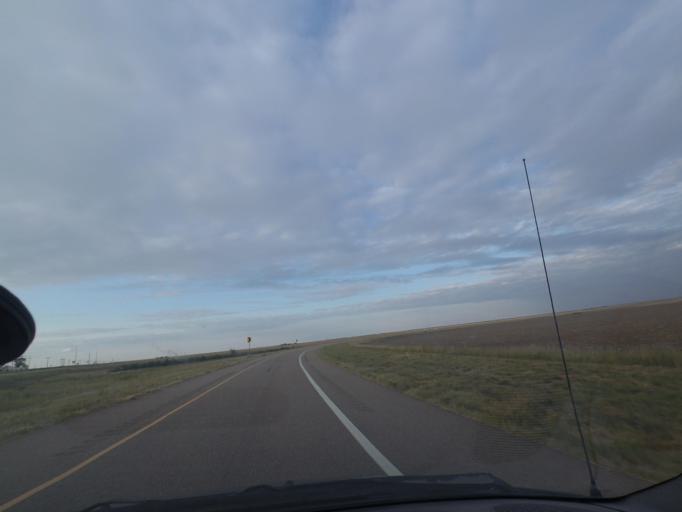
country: US
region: Colorado
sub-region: Yuma County
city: Wray
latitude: 39.7436
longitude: -102.2553
